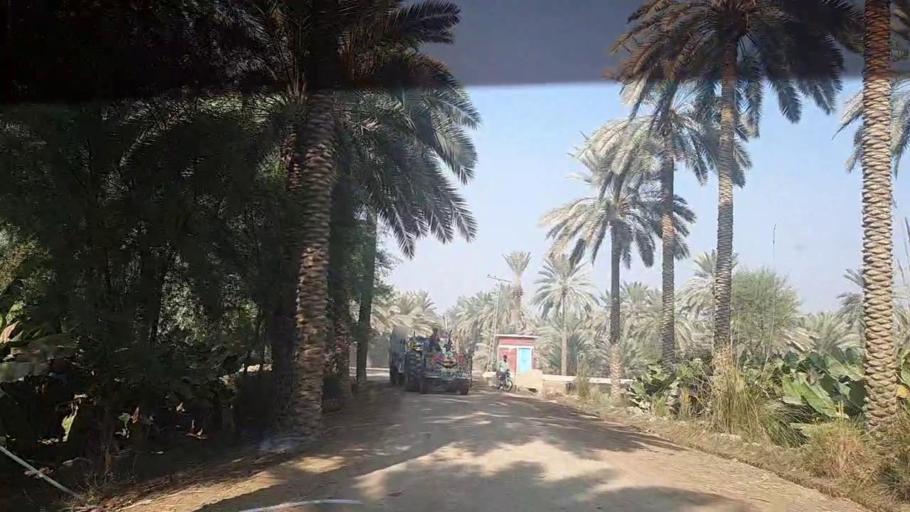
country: PK
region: Sindh
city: Khairpur
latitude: 27.4665
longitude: 68.7166
